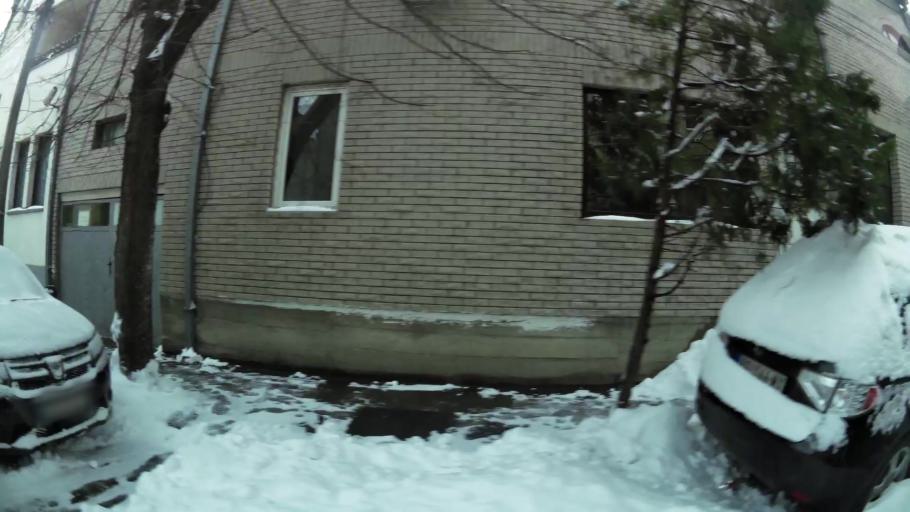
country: RS
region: Central Serbia
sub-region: Belgrade
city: Stari Grad
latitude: 44.8208
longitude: 20.4718
